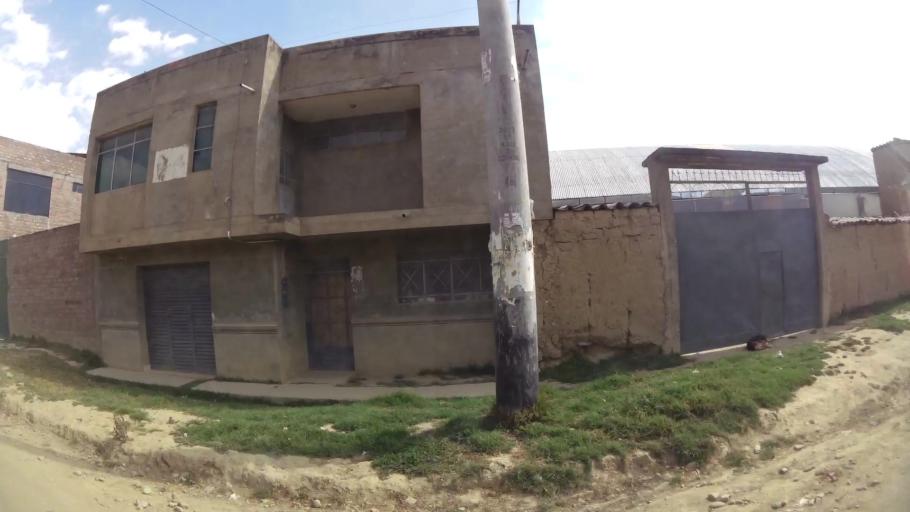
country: PE
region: Junin
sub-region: Provincia de Huancayo
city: Huancayo
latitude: -12.0923
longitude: -75.1977
